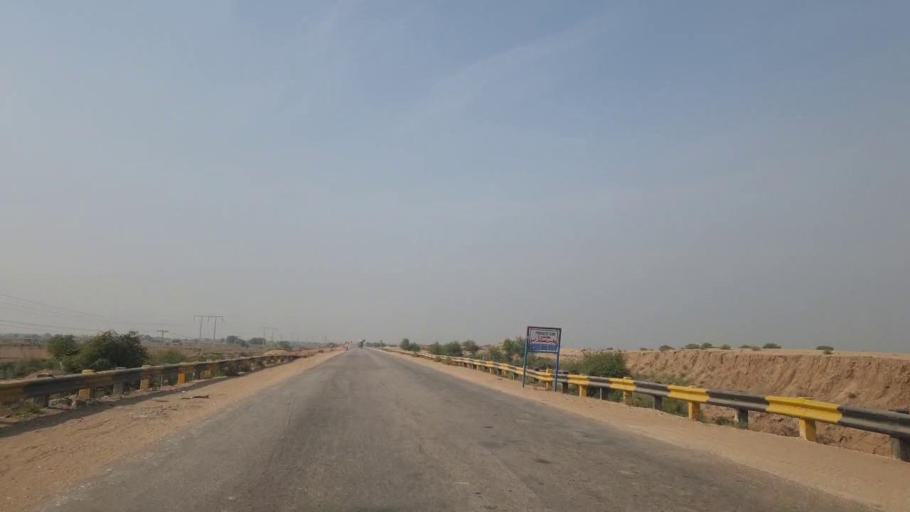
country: PK
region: Sindh
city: Sann
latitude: 26.1413
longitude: 68.0380
